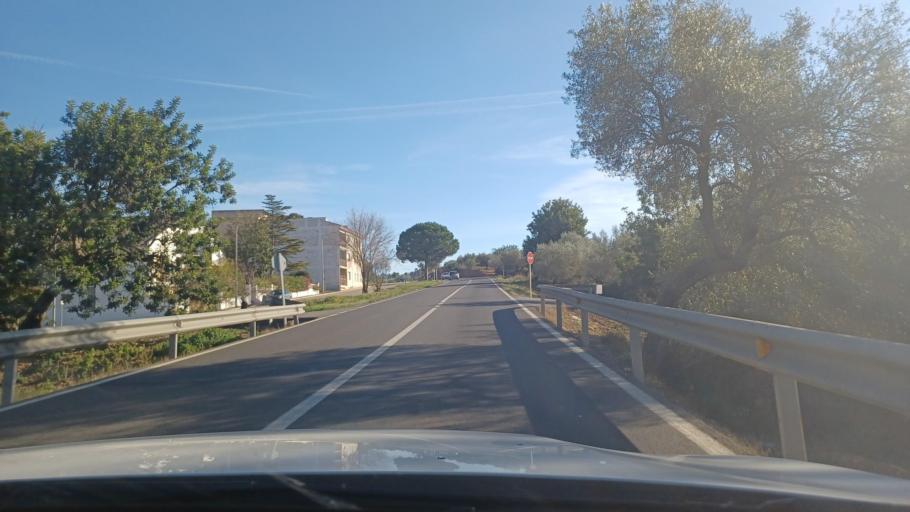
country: ES
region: Catalonia
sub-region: Provincia de Tarragona
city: Masdenverge
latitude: 40.7126
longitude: 0.5335
